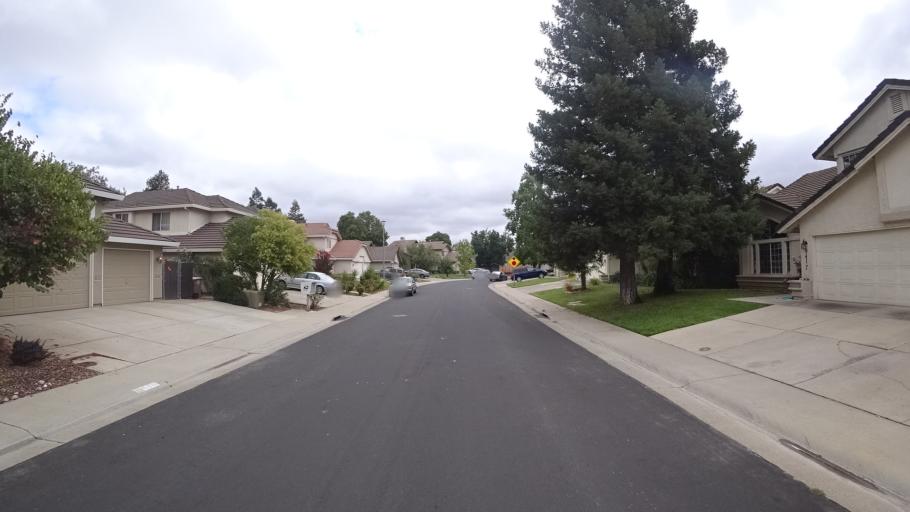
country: US
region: California
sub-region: Sacramento County
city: Laguna
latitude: 38.4159
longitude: -121.4214
